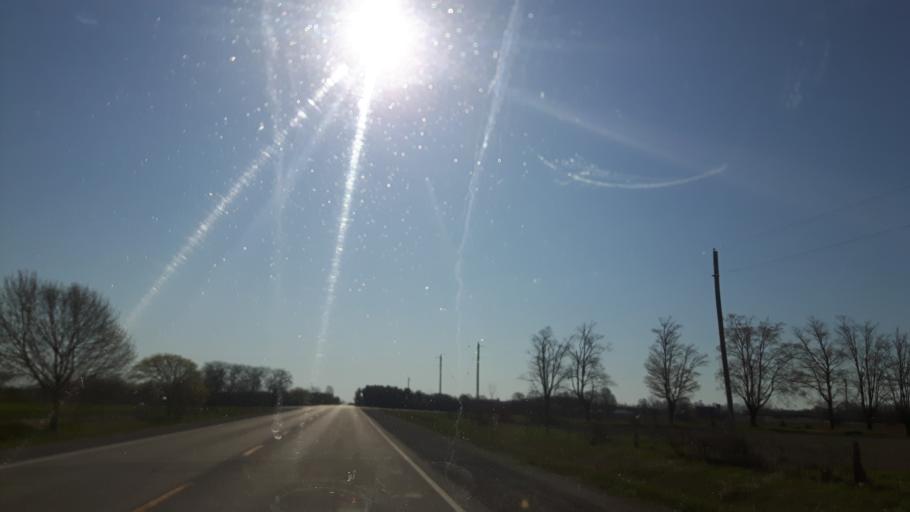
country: CA
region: Ontario
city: Goderich
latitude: 43.6428
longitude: -81.6860
